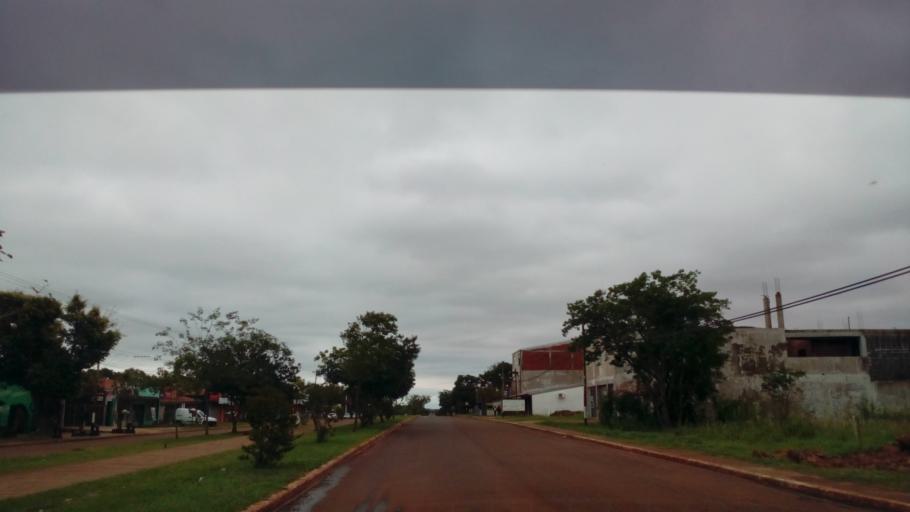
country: AR
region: Misiones
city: Garupa
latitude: -27.4607
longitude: -55.8589
